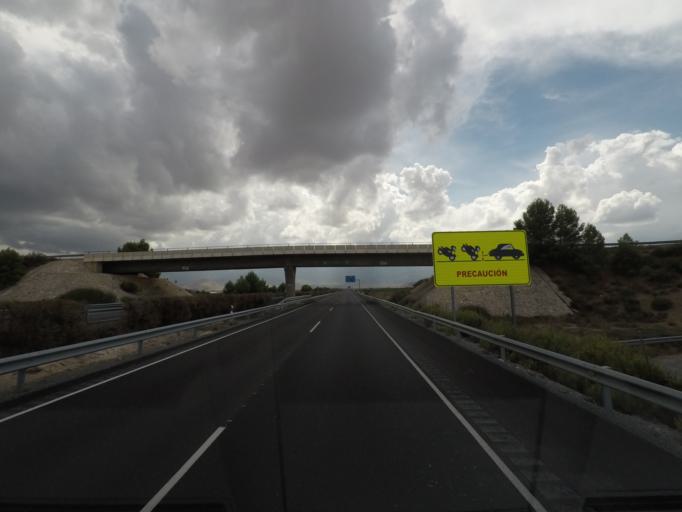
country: ES
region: Andalusia
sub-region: Provincia de Granada
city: Albunan
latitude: 37.2459
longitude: -3.0819
